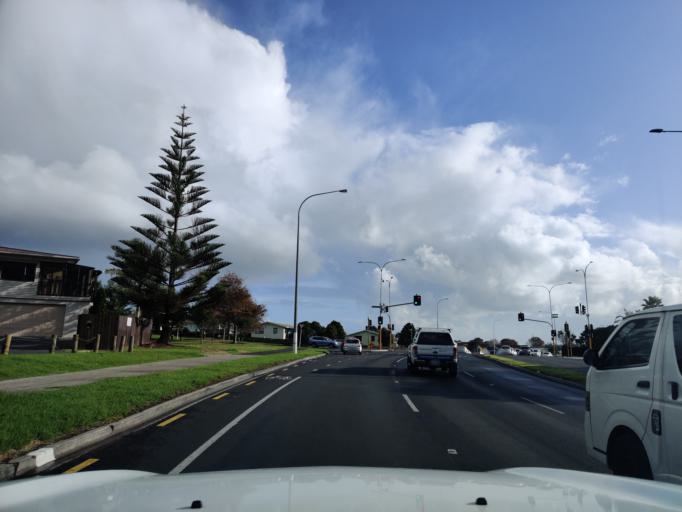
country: NZ
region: Auckland
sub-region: Auckland
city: Manukau City
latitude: -36.9829
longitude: 174.8959
